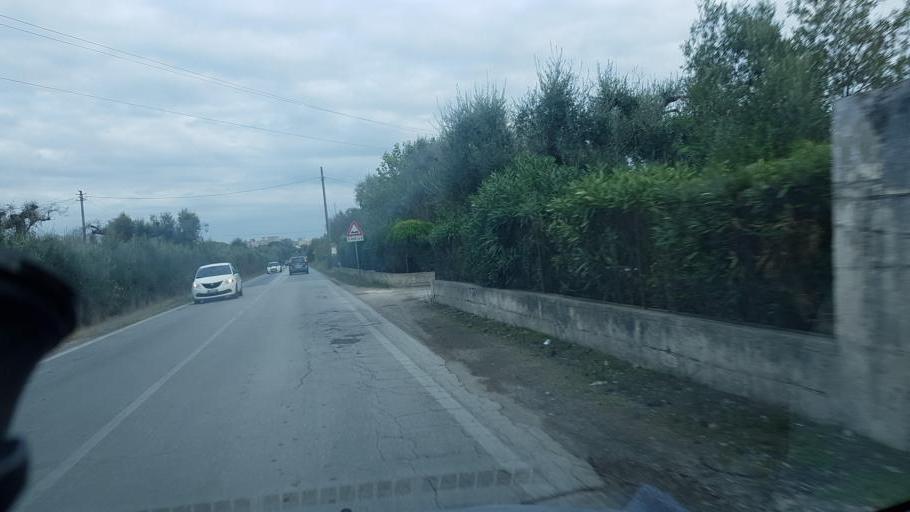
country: IT
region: Apulia
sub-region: Provincia di Brindisi
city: Oria
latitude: 40.5092
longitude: 17.6250
